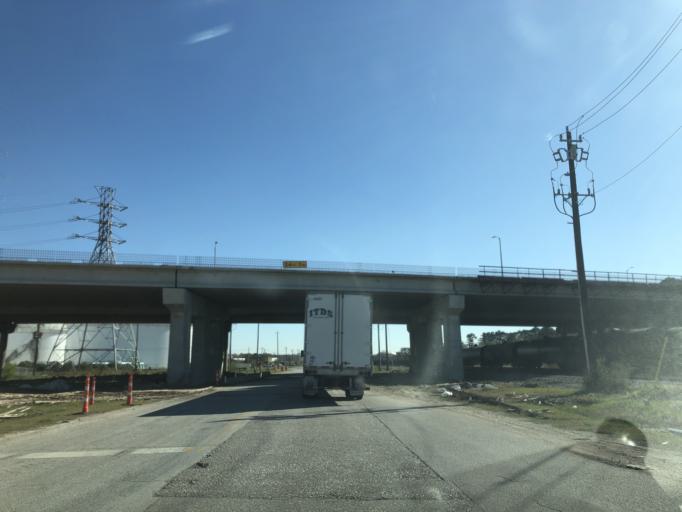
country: US
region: Texas
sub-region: Harris County
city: Cloverleaf
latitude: 29.7553
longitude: -95.1468
